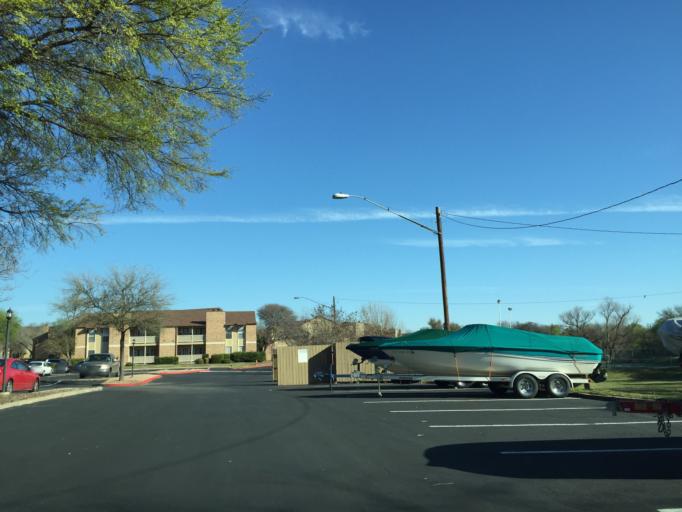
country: US
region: Texas
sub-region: Williamson County
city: Jollyville
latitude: 30.4088
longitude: -97.7425
